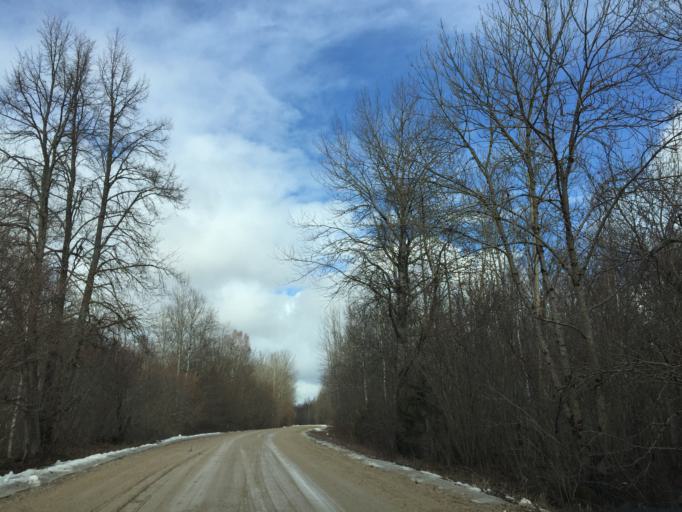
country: EE
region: Laeaene
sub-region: Lihula vald
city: Lihula
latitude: 58.7228
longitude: 23.8298
